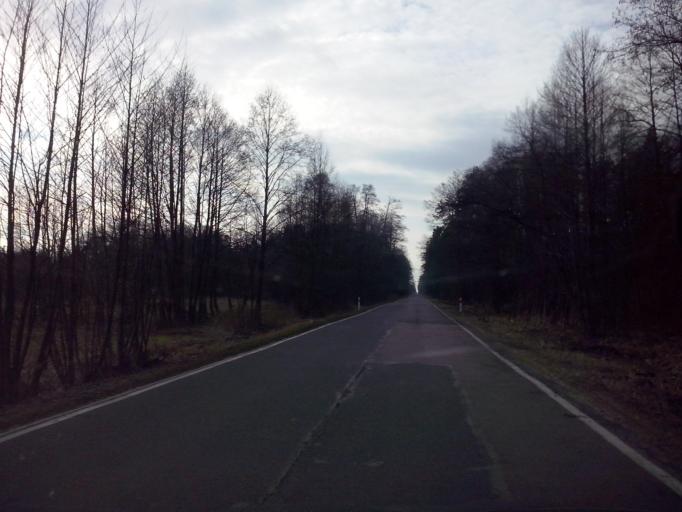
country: PL
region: Subcarpathian Voivodeship
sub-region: Powiat nizanski
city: Harasiuki
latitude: 50.5005
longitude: 22.5372
